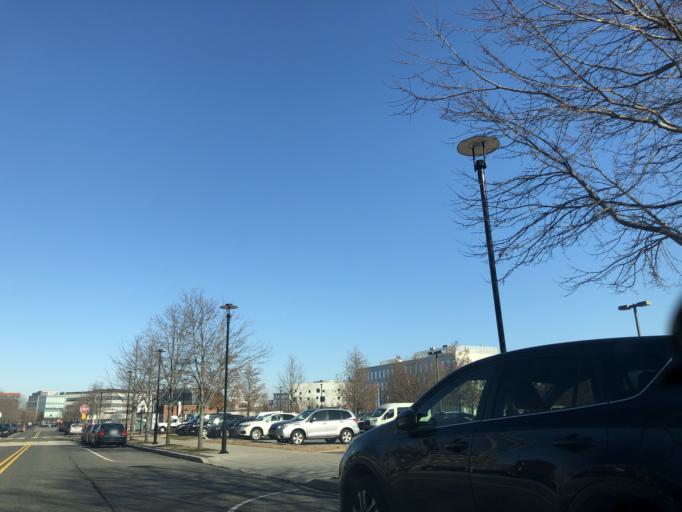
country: US
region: New Jersey
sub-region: Gloucester County
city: National Park
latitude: 39.8921
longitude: -75.1738
